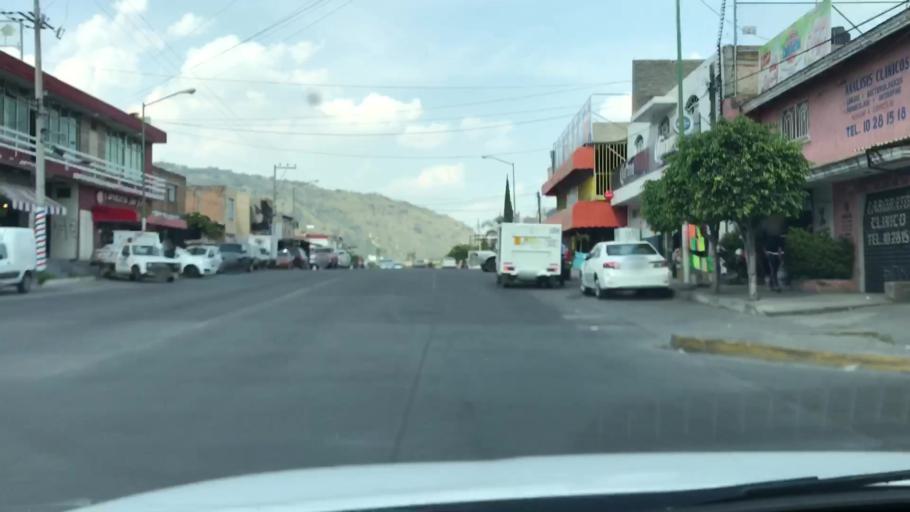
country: MX
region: Jalisco
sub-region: Tlajomulco de Zuniga
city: Palomar
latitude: 20.6350
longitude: -103.4604
